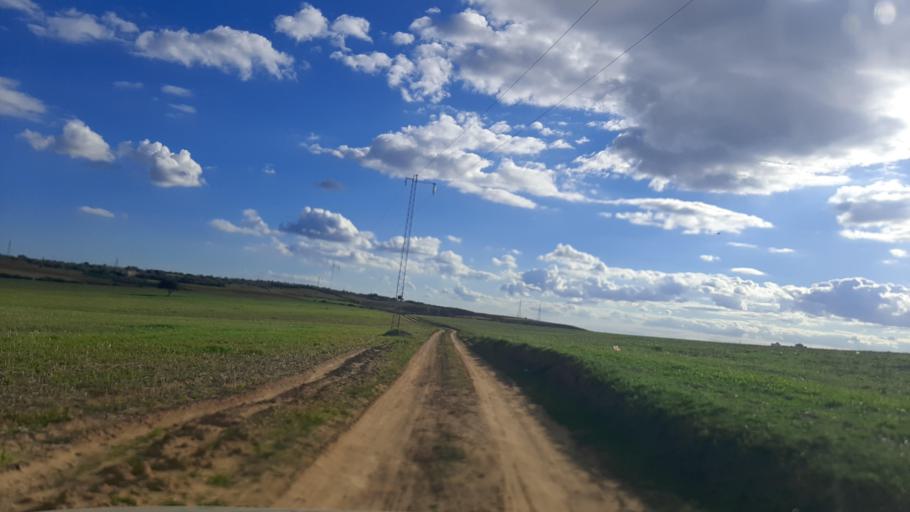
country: TN
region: Nabul
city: Bu `Urqub
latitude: 36.4499
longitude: 10.5011
